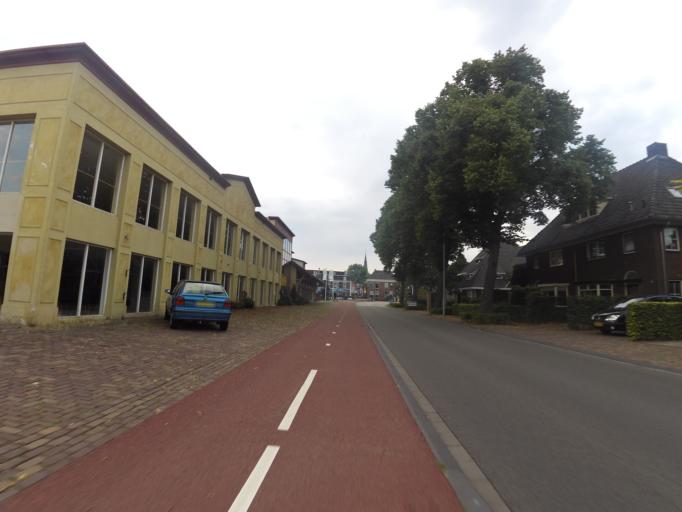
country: NL
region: Gelderland
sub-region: Oude IJsselstreek
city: Gendringen
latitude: 51.8702
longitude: 6.3807
